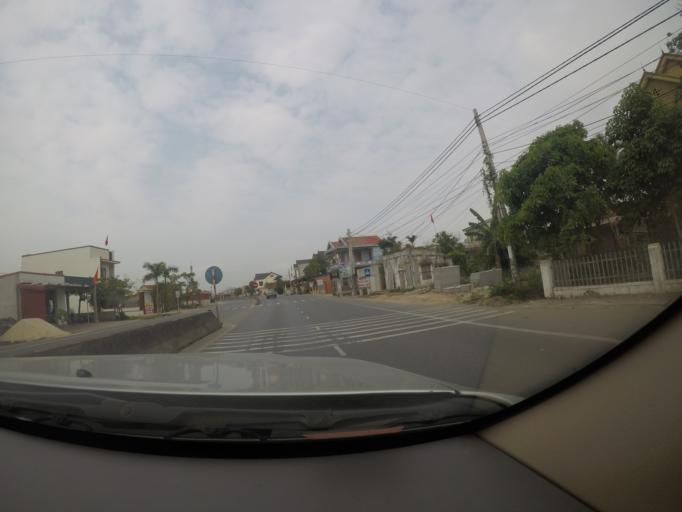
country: VN
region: Quang Binh
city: Ba Don
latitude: 17.8756
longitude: 106.4402
